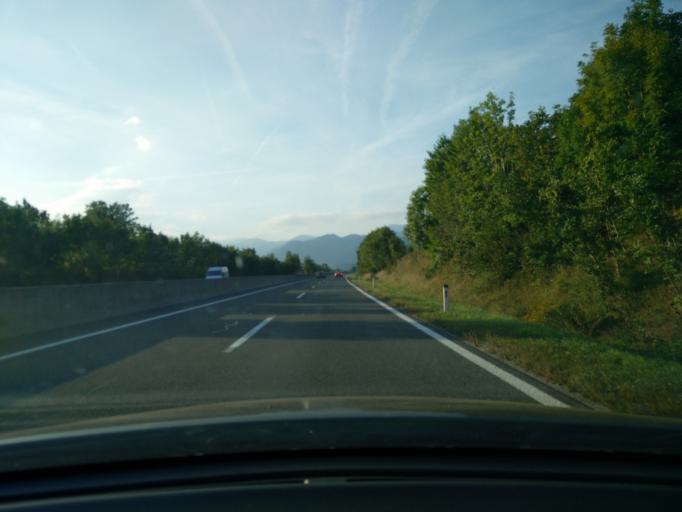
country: SI
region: Zirovnica
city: Zirovnica
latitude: 46.3871
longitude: 14.1403
